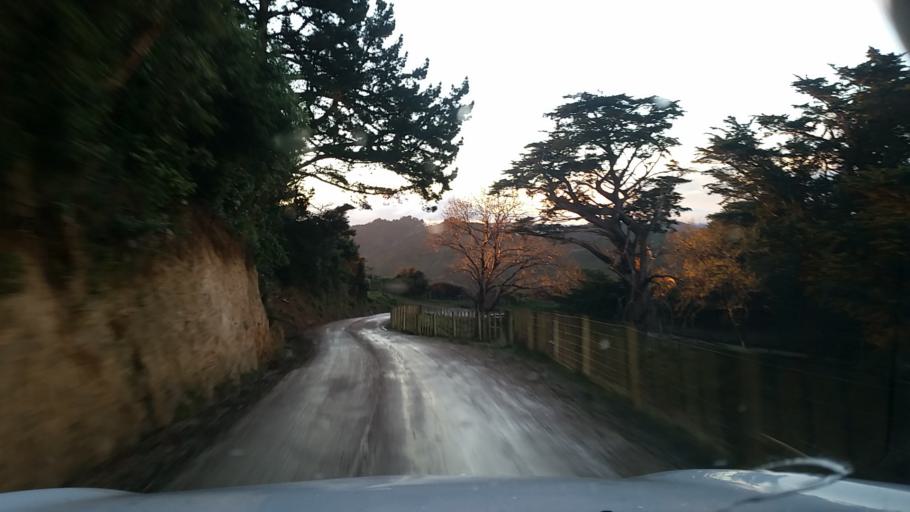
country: NZ
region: Manawatu-Wanganui
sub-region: Wanganui District
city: Wanganui
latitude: -39.7676
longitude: 174.8719
